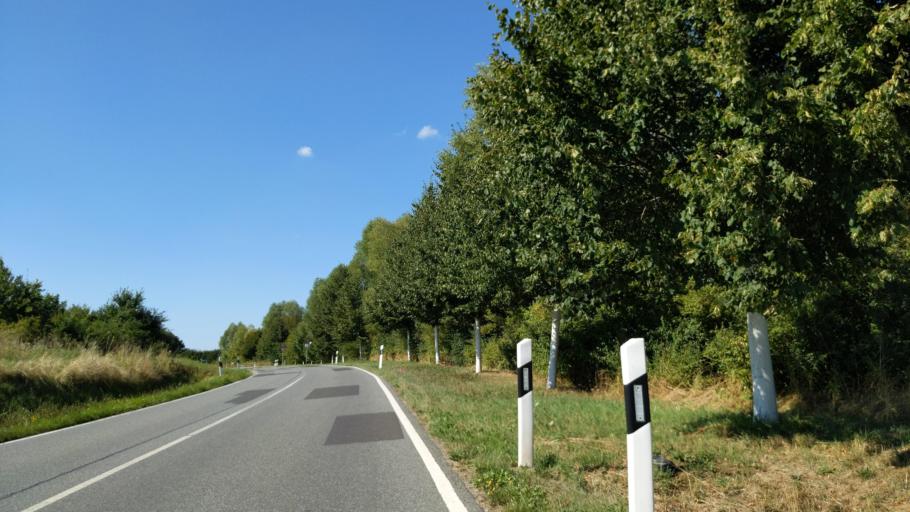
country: DE
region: Mecklenburg-Vorpommern
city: Selmsdorf
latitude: 53.8382
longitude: 10.9167
